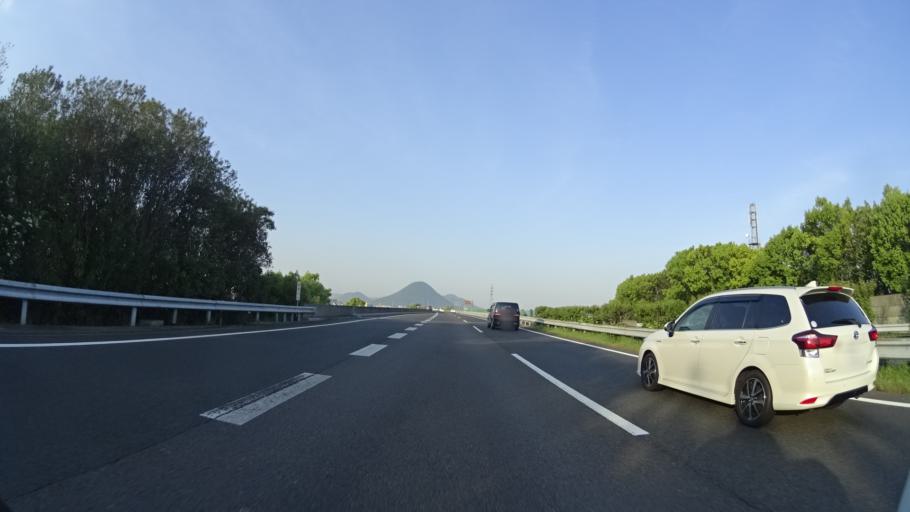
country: JP
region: Kagawa
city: Marugame
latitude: 34.2435
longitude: 133.7887
